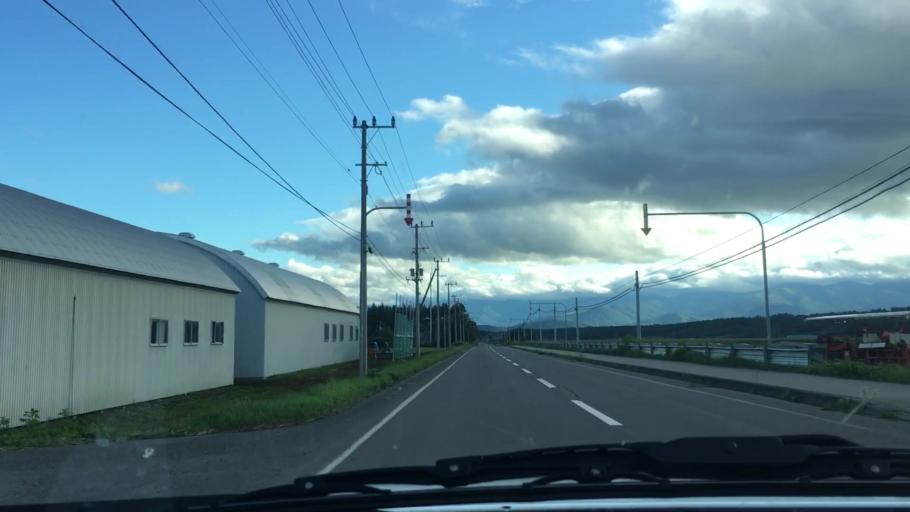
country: JP
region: Hokkaido
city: Otofuke
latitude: 43.1472
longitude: 142.8986
